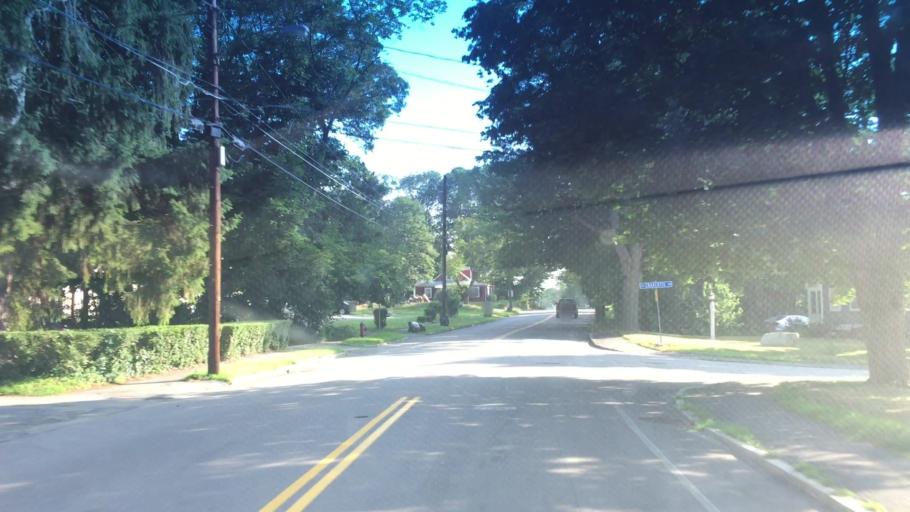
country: US
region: Massachusetts
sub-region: Norfolk County
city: Norwood
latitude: 42.1629
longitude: -71.2093
